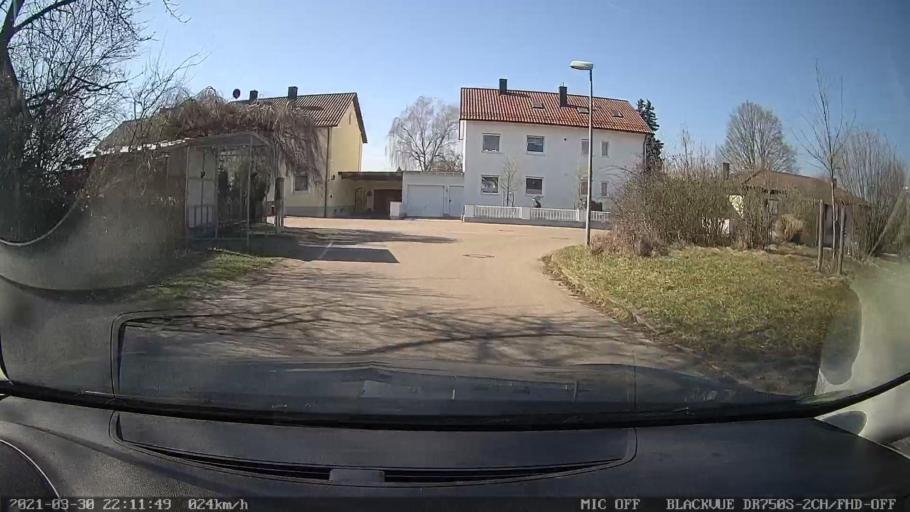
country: DE
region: Bavaria
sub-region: Upper Palatinate
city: Zeitlarn
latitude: 49.0881
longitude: 12.1231
